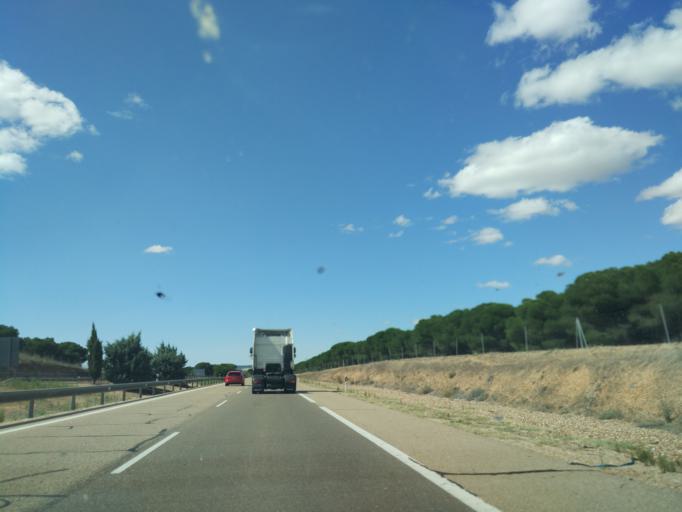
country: ES
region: Castille and Leon
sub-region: Provincia de Valladolid
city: Rueda
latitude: 41.4505
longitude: -4.9796
